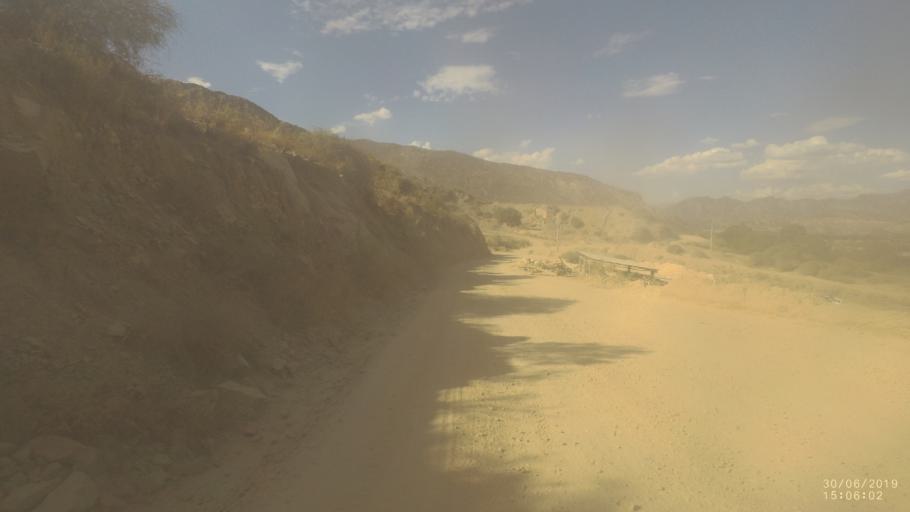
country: BO
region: Cochabamba
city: Irpa Irpa
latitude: -17.7321
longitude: -66.3135
